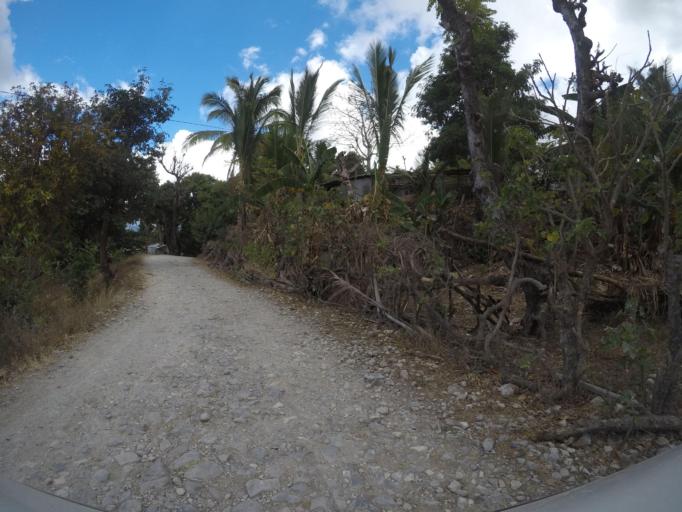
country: TL
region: Baucau
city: Baucau
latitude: -8.5203
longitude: 126.6940
